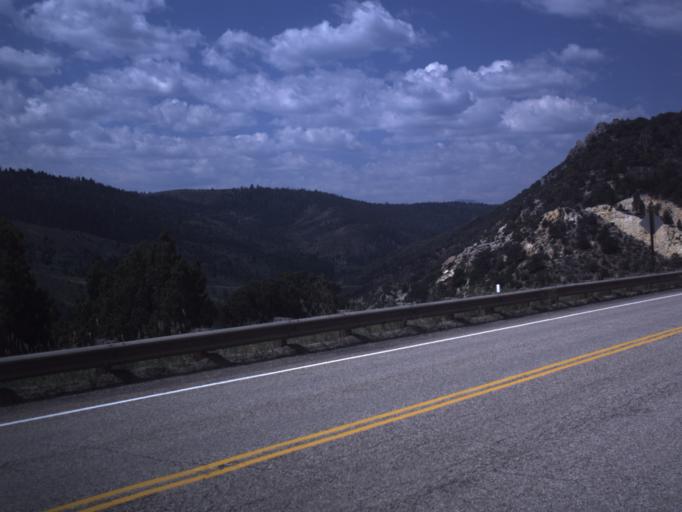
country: US
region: Utah
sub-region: Daggett County
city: Manila
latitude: 40.8976
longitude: -109.7091
